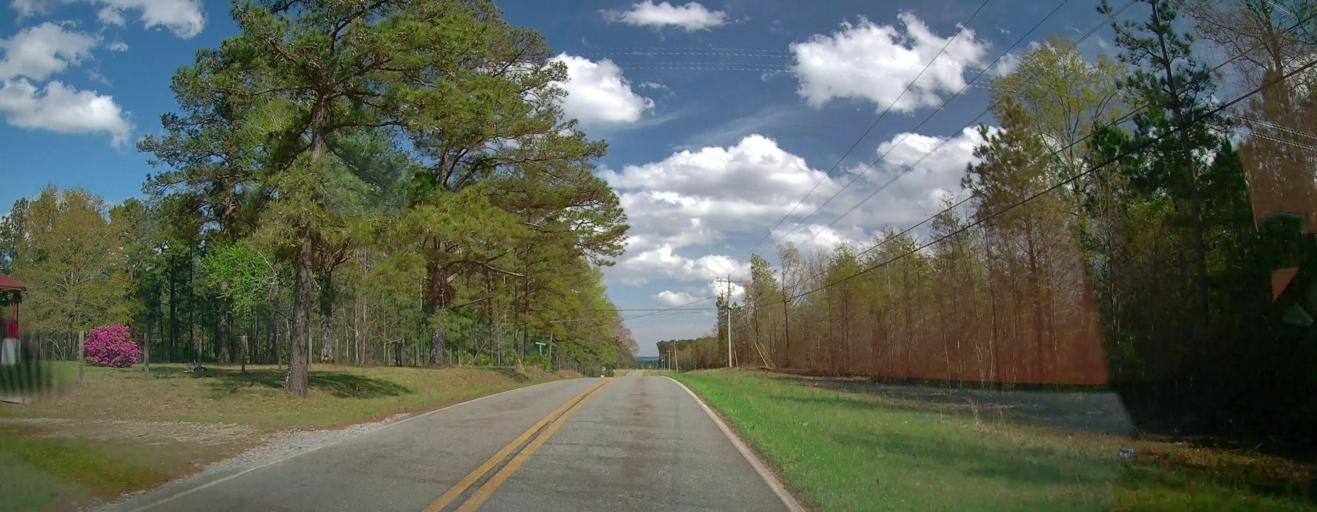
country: US
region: Georgia
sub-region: Wilkinson County
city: Gordon
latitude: 32.8063
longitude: -83.4418
